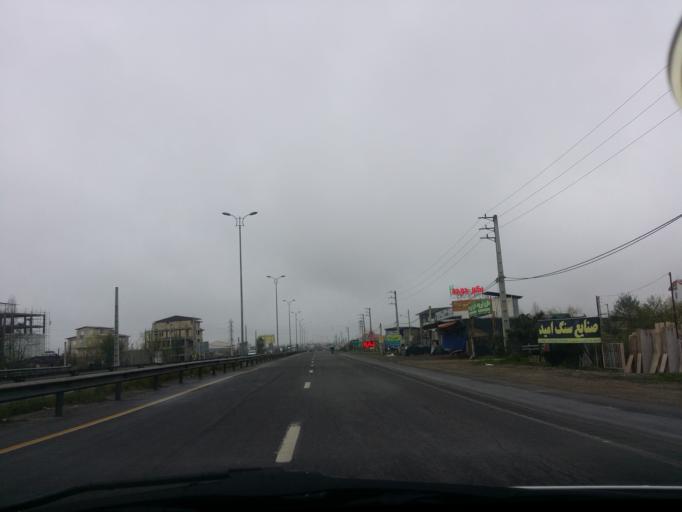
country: IR
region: Mazandaran
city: Tonekabon
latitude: 36.7961
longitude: 50.9081
